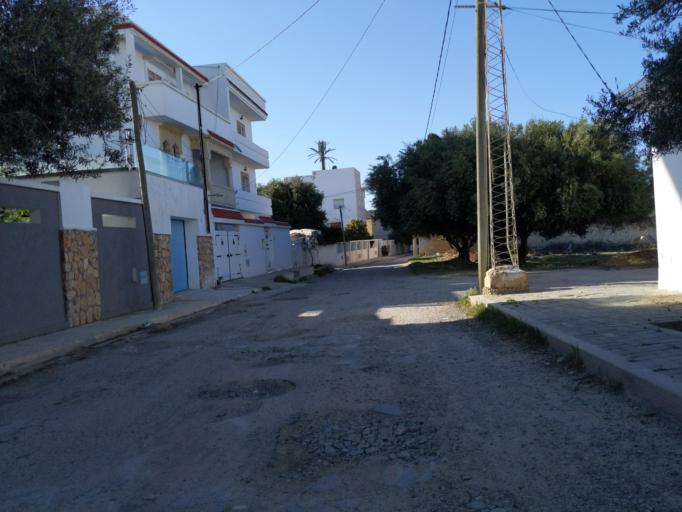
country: TN
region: Al Munastir
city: Saqanis
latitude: 35.7770
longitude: 10.7983
